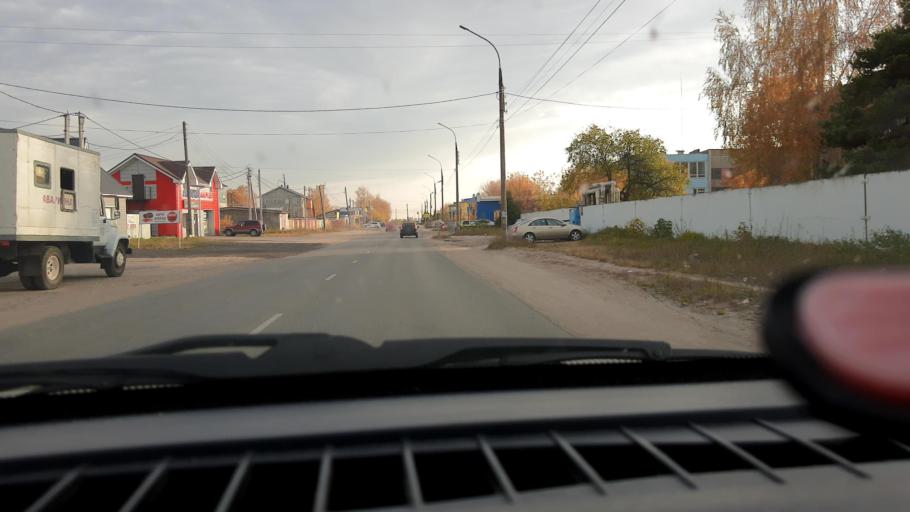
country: RU
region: Nizjnij Novgorod
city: Gorodets
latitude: 56.6434
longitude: 43.4893
